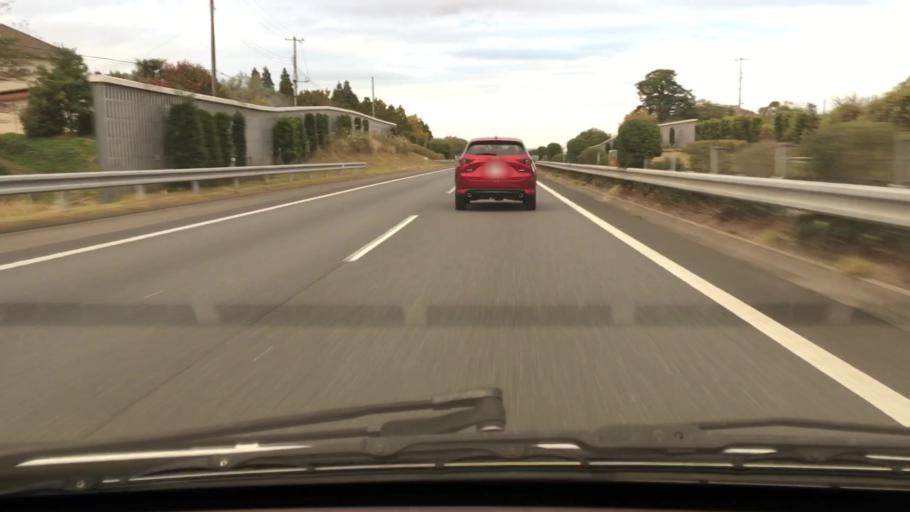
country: JP
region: Chiba
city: Ichihara
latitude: 35.4719
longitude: 140.0834
